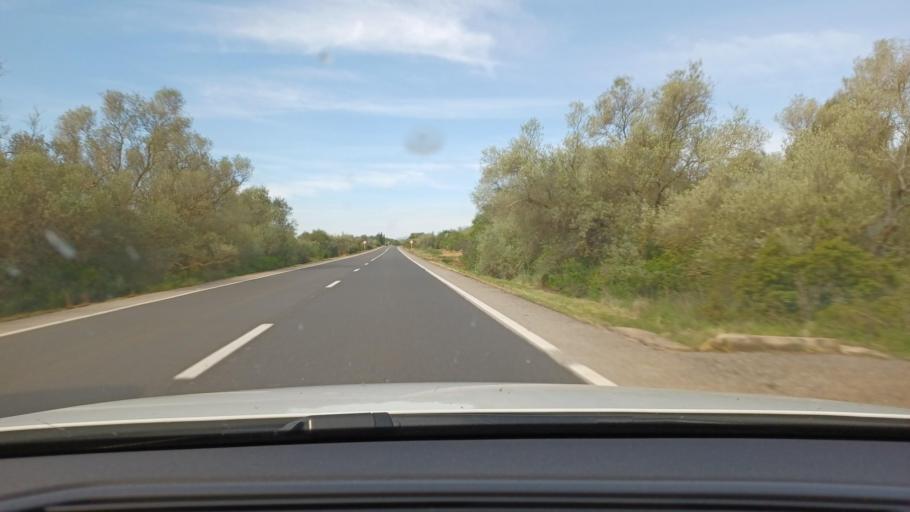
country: ES
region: Catalonia
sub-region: Provincia de Tarragona
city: Ulldecona
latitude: 40.6510
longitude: 0.3946
